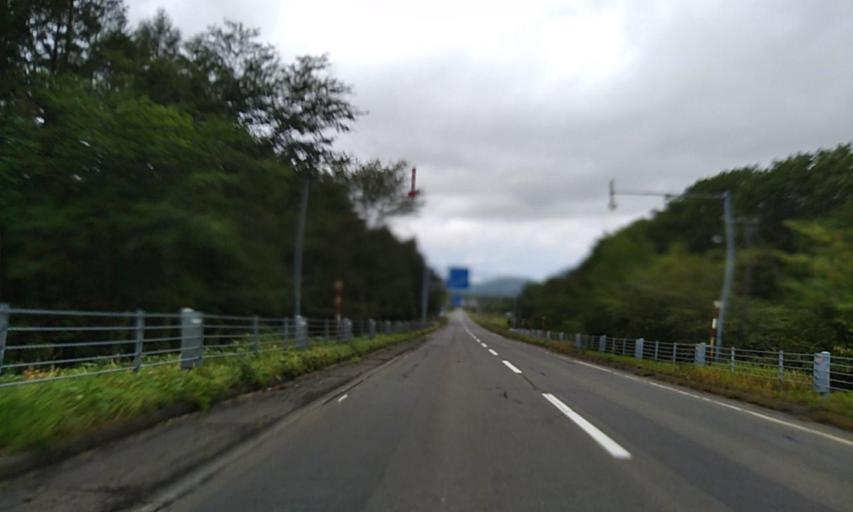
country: JP
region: Hokkaido
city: Bihoro
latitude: 43.5149
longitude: 144.4348
